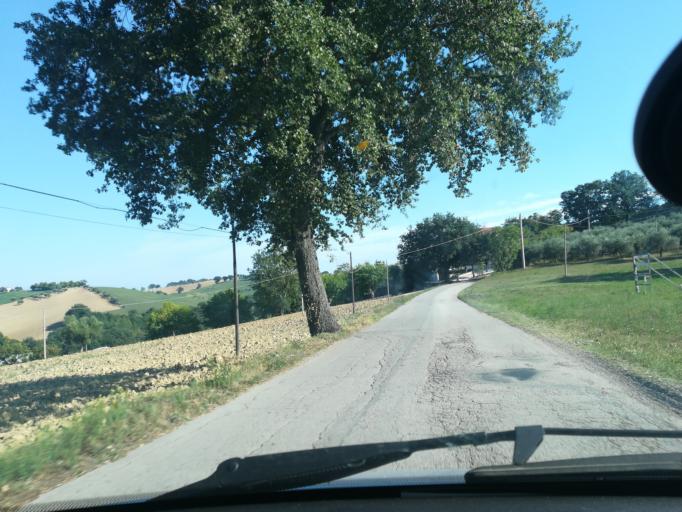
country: IT
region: The Marches
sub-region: Provincia di Macerata
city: Macerata
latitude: 43.3074
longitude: 13.4763
